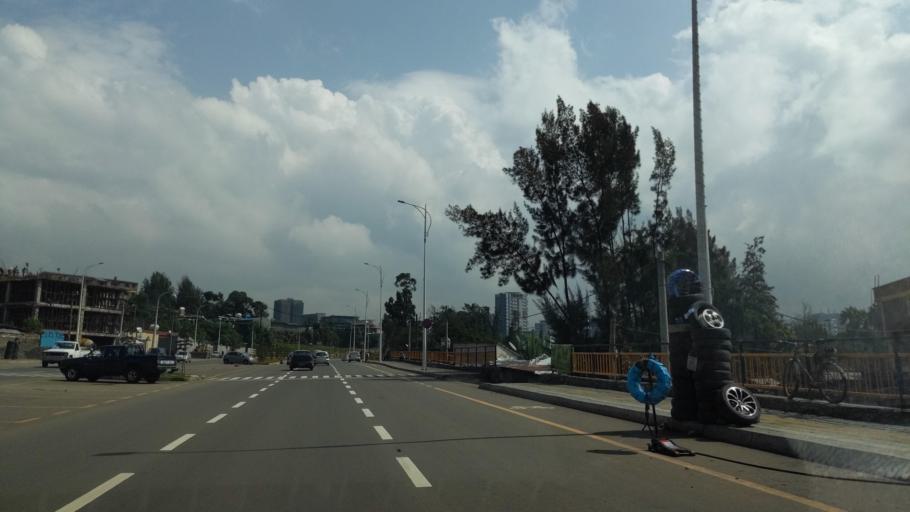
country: ET
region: Adis Abeba
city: Addis Ababa
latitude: 9.0027
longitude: 38.7736
